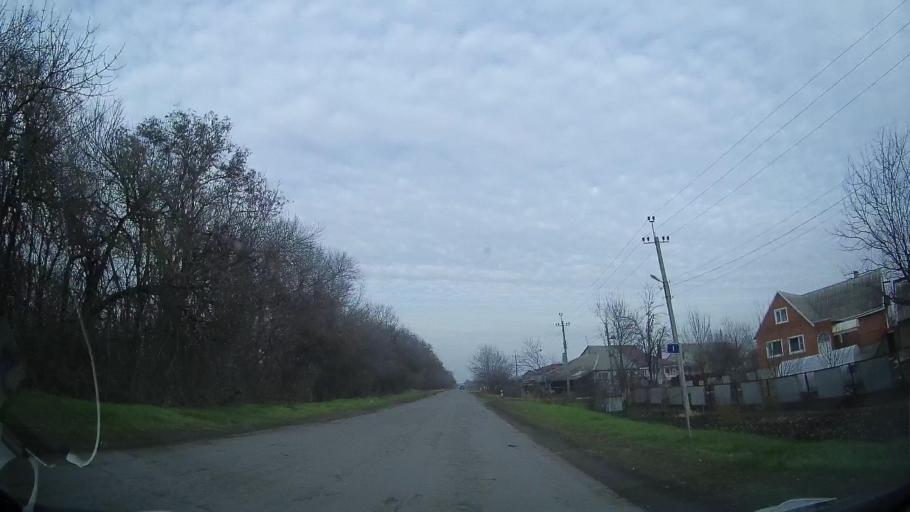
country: RU
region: Rostov
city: Zernograd
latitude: 46.8656
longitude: 40.3265
